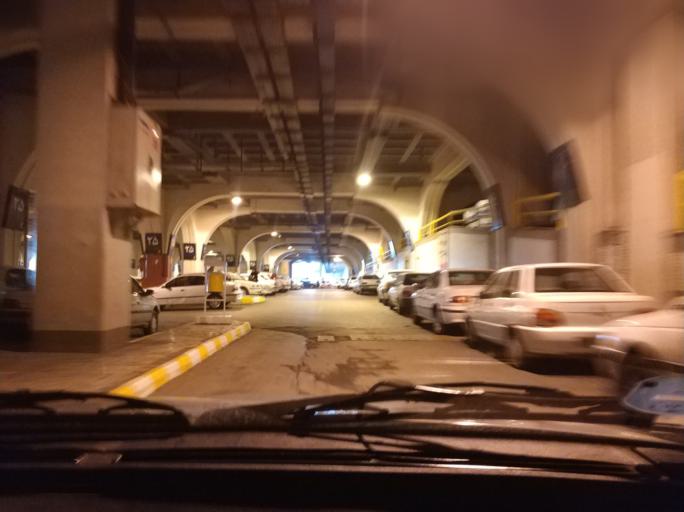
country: IR
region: Razavi Khorasan
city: Mashhad
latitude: 36.2866
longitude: 59.6183
